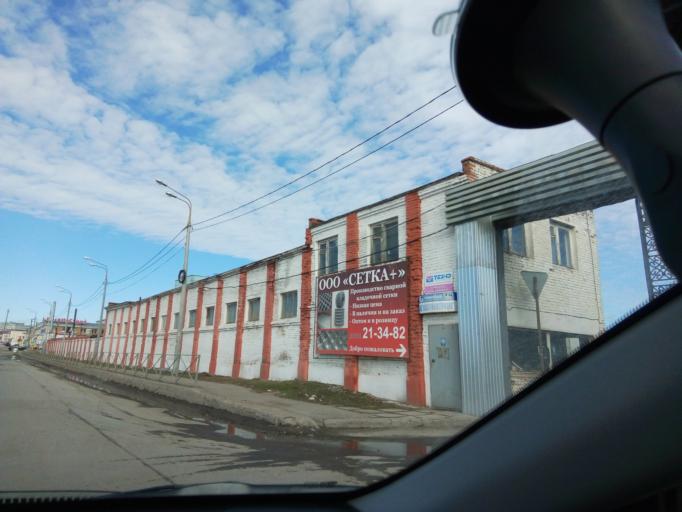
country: RU
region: Chuvashia
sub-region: Cheboksarskiy Rayon
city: Cheboksary
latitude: 56.1037
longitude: 47.2510
